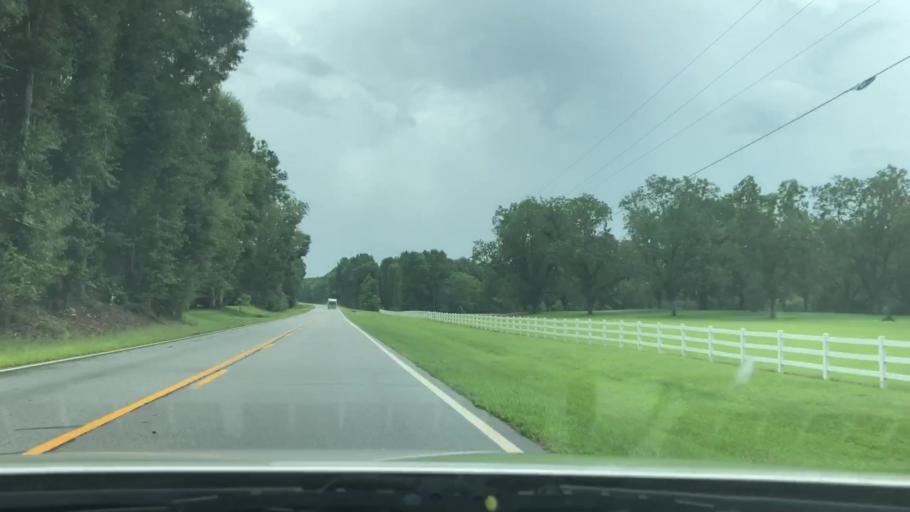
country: US
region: Georgia
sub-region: Pike County
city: Zebulon
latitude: 33.0868
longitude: -84.2707
